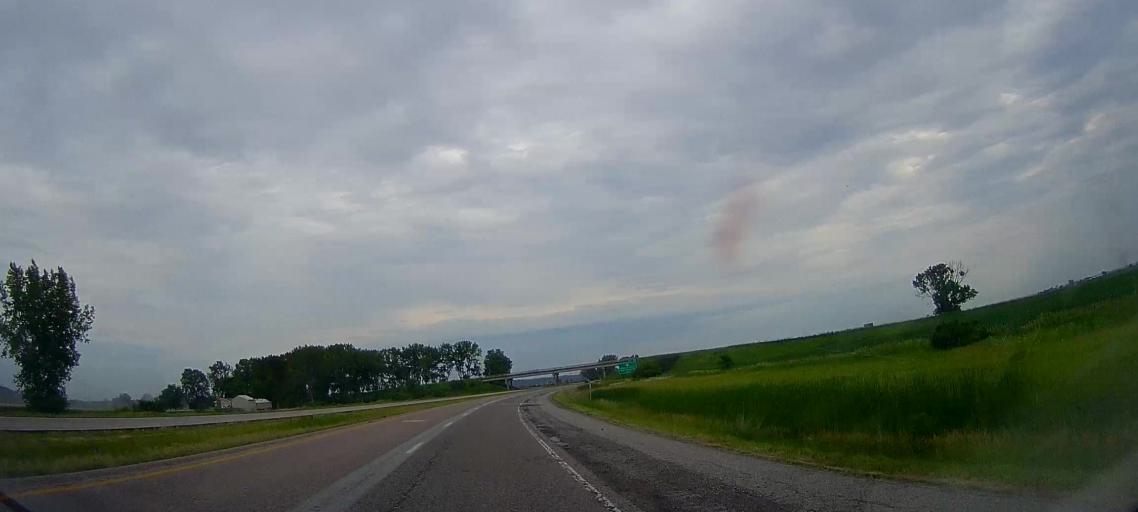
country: US
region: Iowa
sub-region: Harrison County
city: Missouri Valley
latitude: 41.5669
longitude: -95.9189
